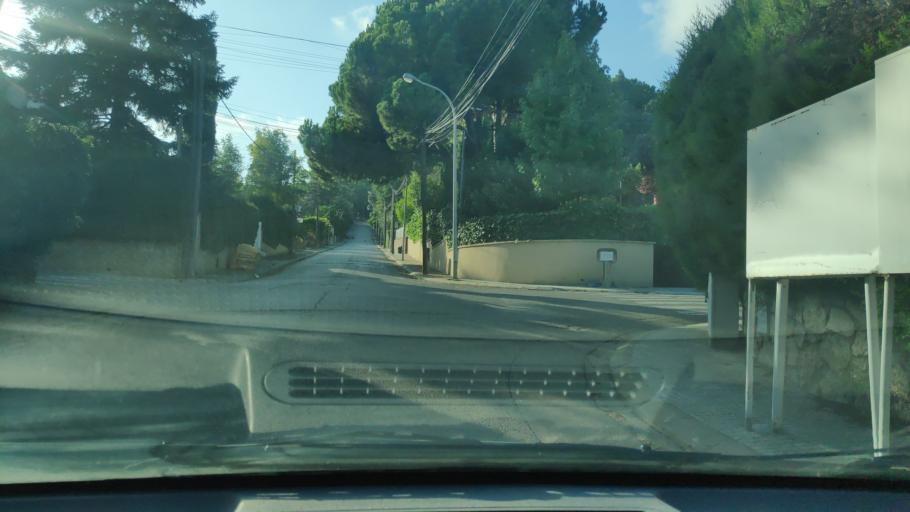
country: ES
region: Catalonia
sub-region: Provincia de Barcelona
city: Sant Quirze del Valles
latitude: 41.5012
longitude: 2.0831
